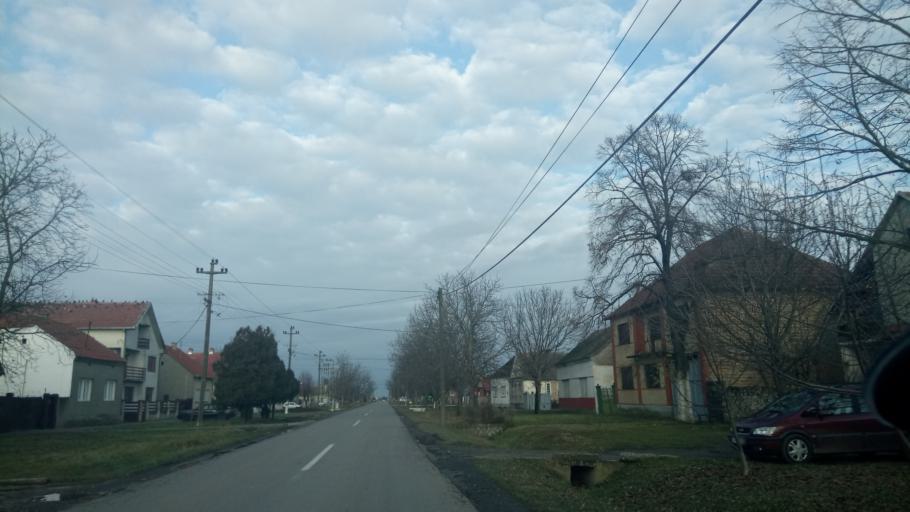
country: RS
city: Vojka
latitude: 44.9394
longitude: 20.1689
